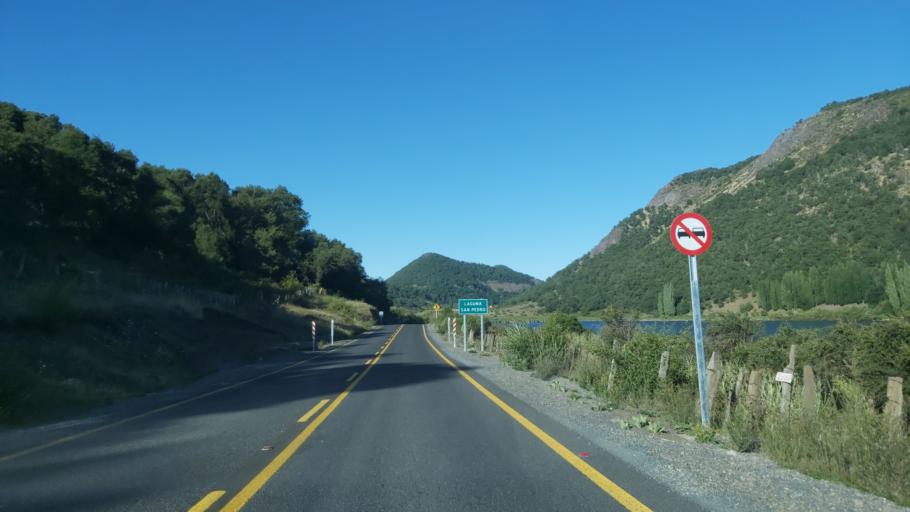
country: AR
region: Neuquen
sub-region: Departamento de Loncopue
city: Loncopue
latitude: -38.4413
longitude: -71.3373
